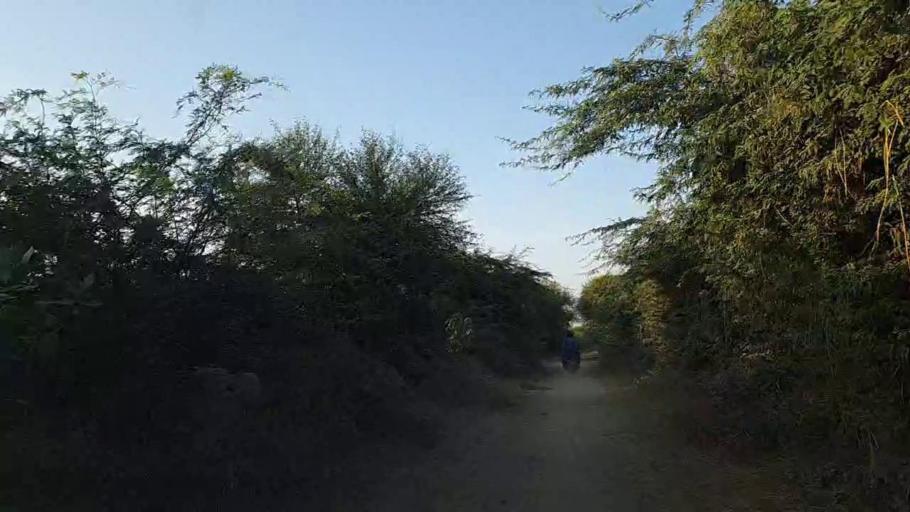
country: PK
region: Sindh
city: Mirpur Batoro
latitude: 24.7173
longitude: 68.2145
